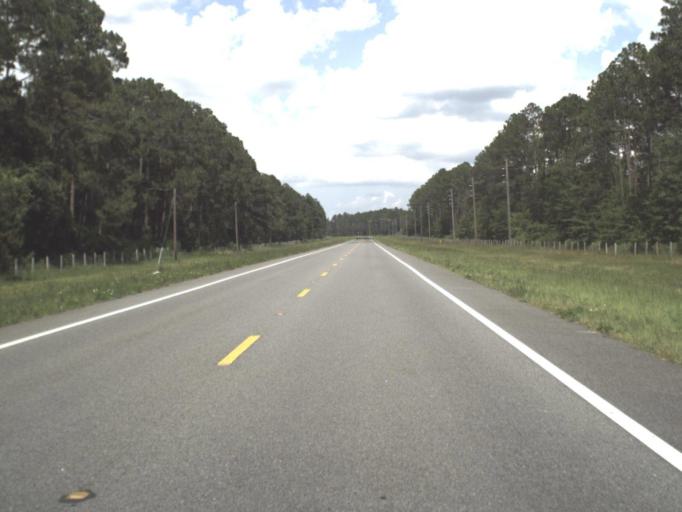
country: US
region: Florida
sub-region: Bradford County
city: Starke
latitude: 29.9568
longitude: -82.0440
